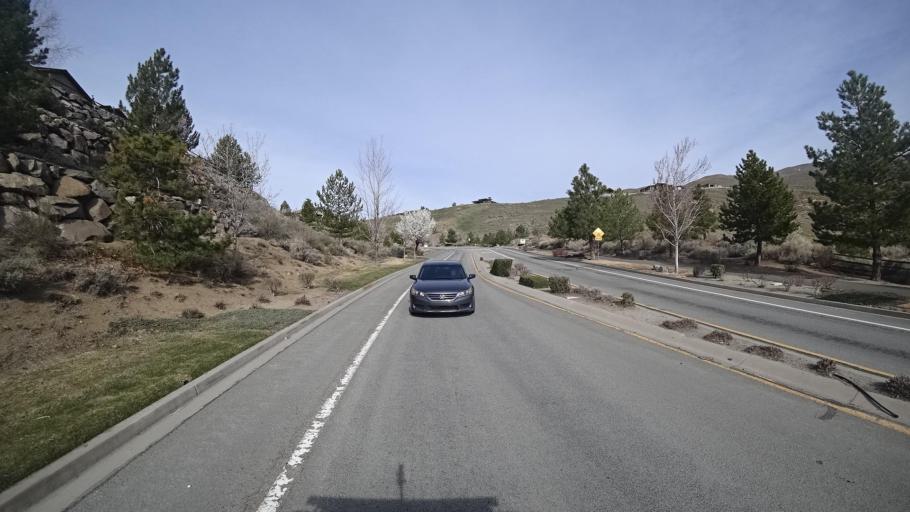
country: US
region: Nevada
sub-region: Washoe County
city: Mogul
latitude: 39.5364
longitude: -119.9306
